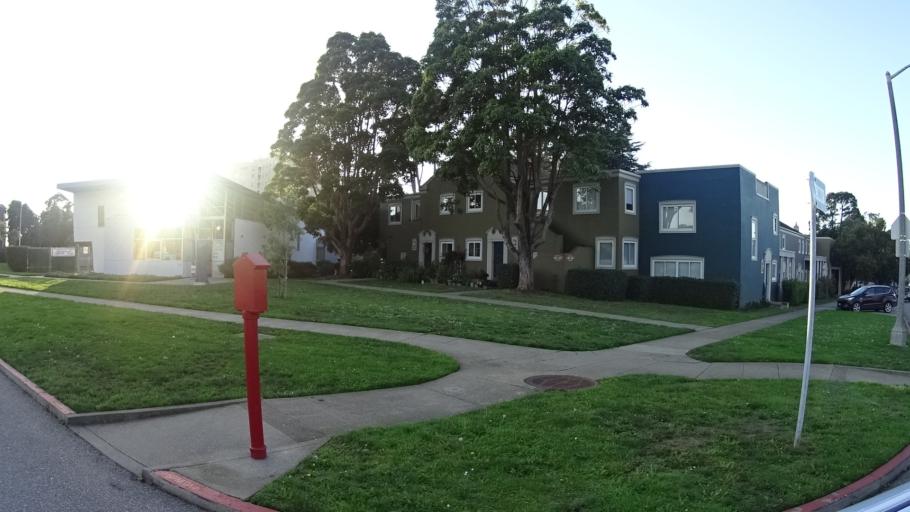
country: US
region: California
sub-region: San Mateo County
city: Daly City
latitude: 37.7185
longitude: -122.4787
